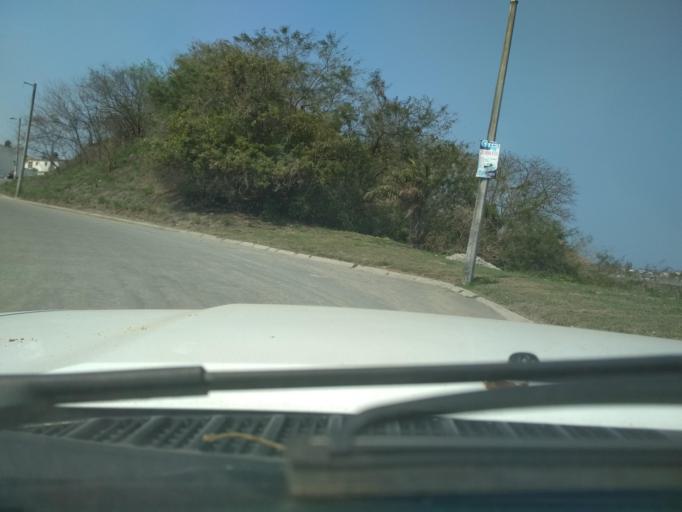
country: MX
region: Veracruz
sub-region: Veracruz
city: Los Torrentes
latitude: 19.1982
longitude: -96.2074
